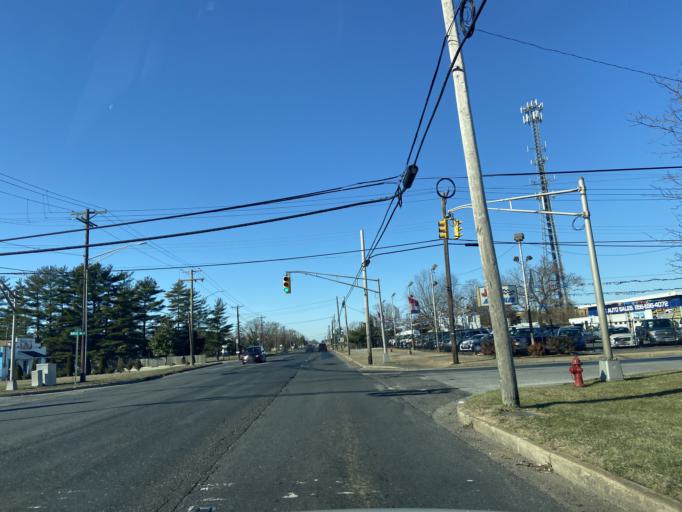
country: US
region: New Jersey
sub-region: Cumberland County
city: Vineland
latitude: 39.4879
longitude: -75.0612
